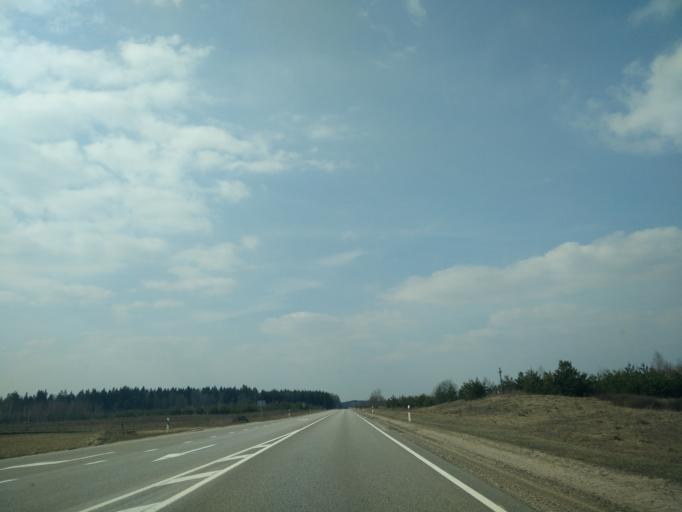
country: LT
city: Lentvaris
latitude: 54.6209
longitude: 25.0549
